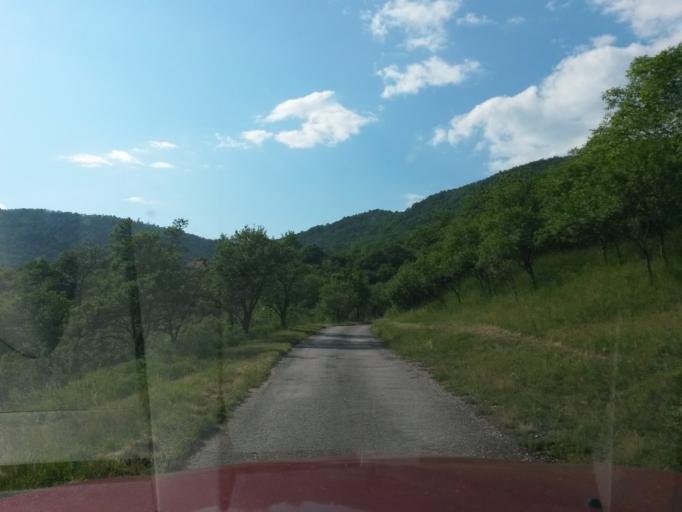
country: SK
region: Kosicky
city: Roznava
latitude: 48.5968
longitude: 20.6539
